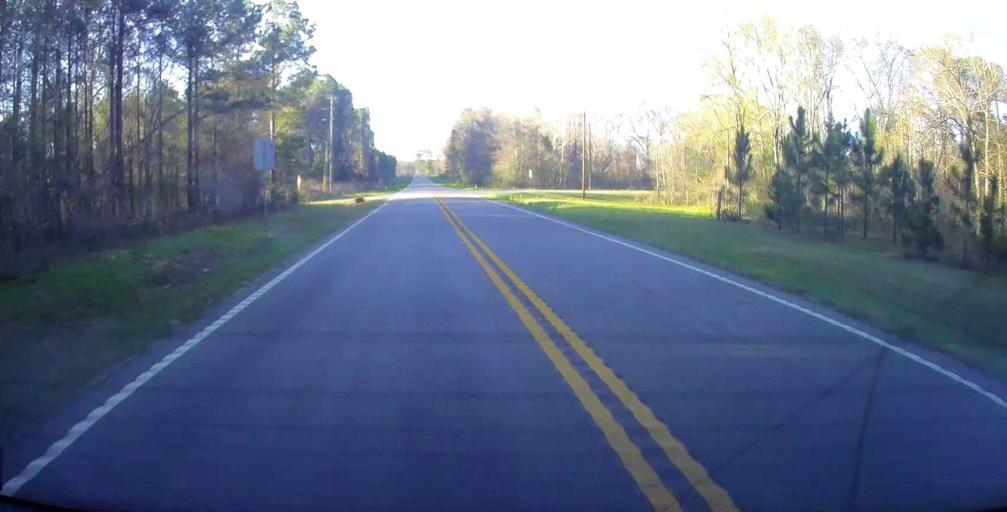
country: US
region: Georgia
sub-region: Pulaski County
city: Hawkinsville
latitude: 32.2022
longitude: -83.3747
